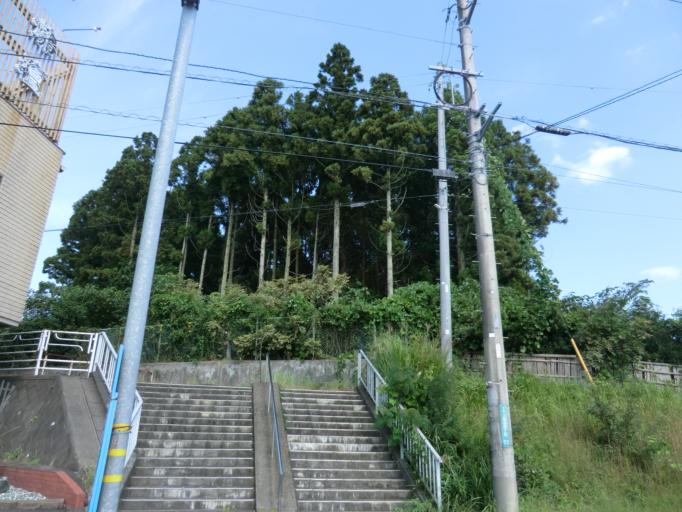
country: JP
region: Ibaraki
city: Ushiku
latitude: 35.9833
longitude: 140.1601
